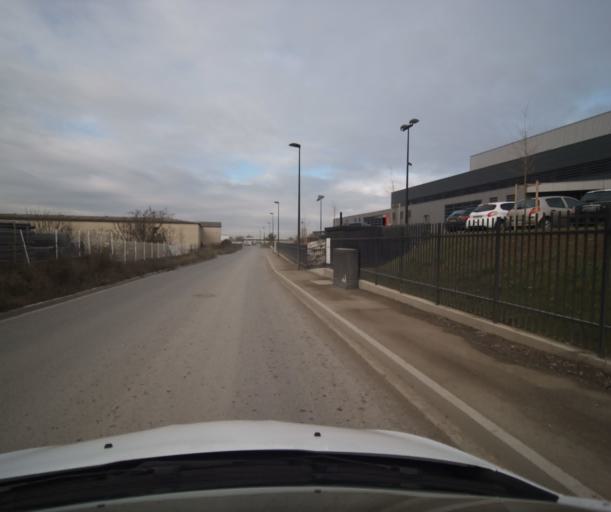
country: FR
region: Midi-Pyrenees
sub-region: Departement de la Haute-Garonne
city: Lespinasse
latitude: 43.7155
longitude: 1.3977
